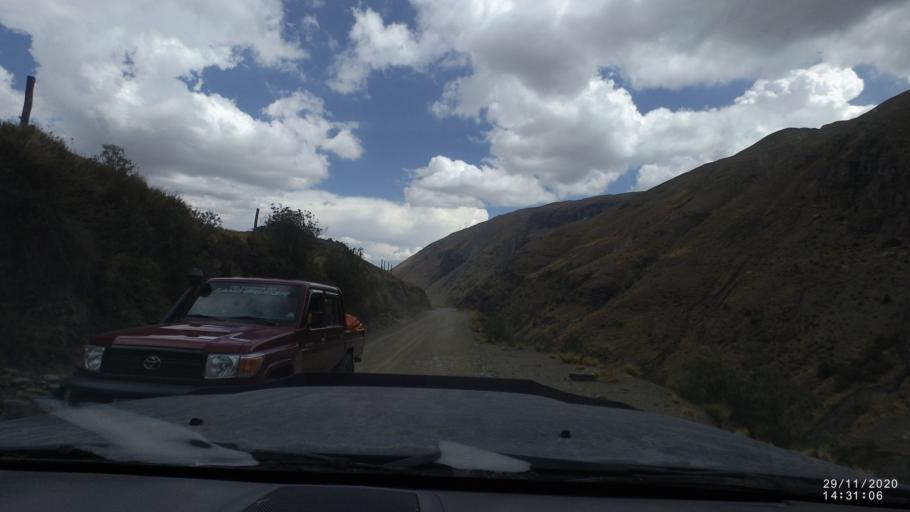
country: BO
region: Cochabamba
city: Sipe Sipe
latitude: -17.2654
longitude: -66.3459
